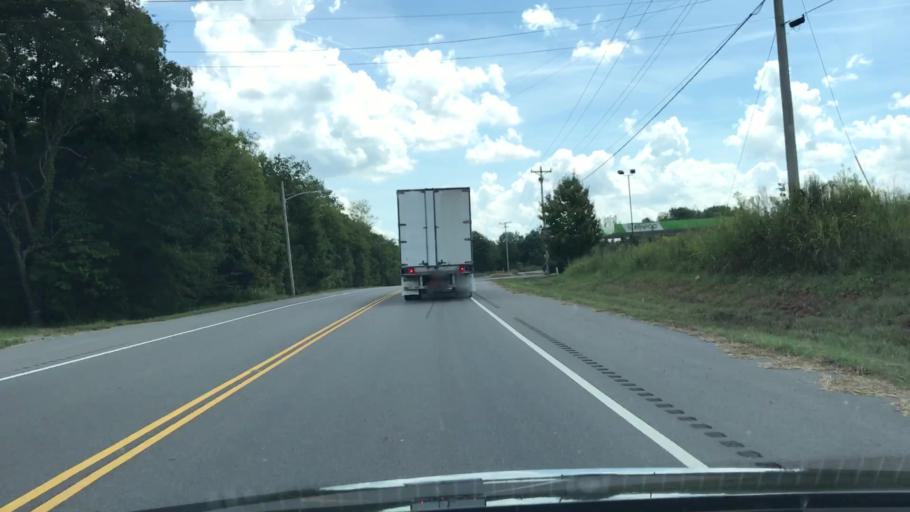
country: US
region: Tennessee
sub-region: Robertson County
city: Cross Plains
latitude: 36.5308
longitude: -86.6485
